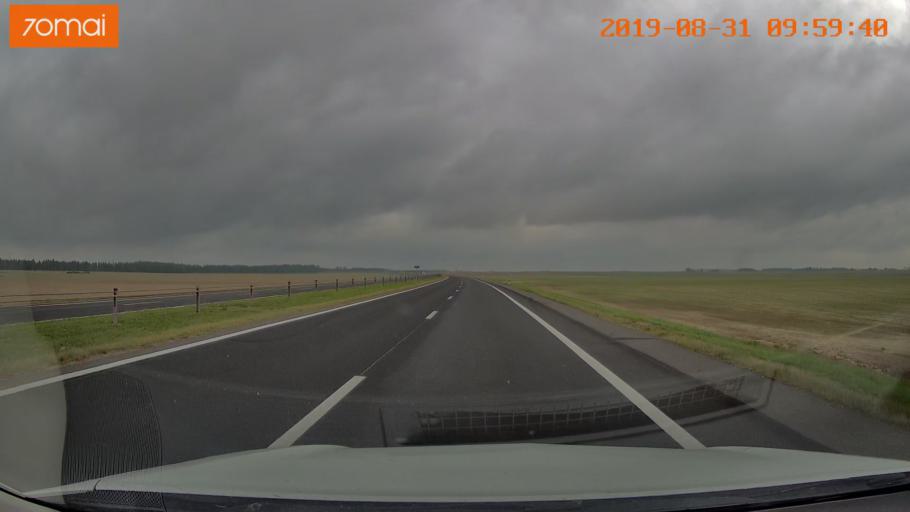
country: BY
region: Mogilev
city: Vishow
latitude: 53.9729
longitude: 29.9973
